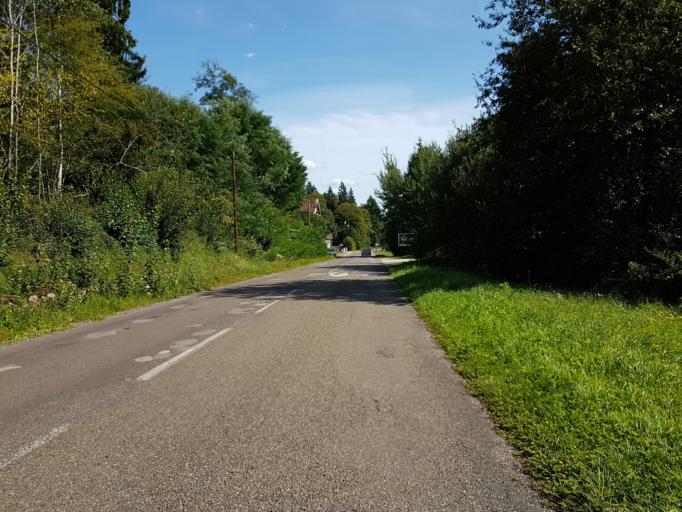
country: FR
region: Franche-Comte
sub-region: Departement de la Haute-Saone
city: Luxeuil-les-Bains
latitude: 47.8268
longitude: 6.3649
